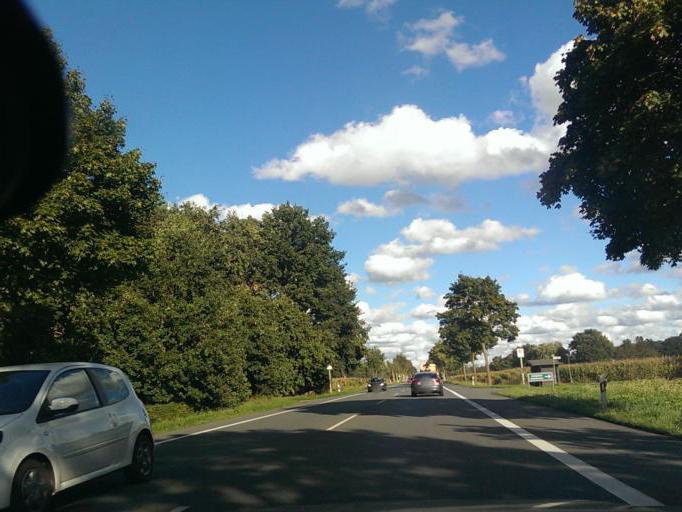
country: DE
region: North Rhine-Westphalia
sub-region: Regierungsbezirk Detmold
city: Delbruck
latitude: 51.7623
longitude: 8.6145
